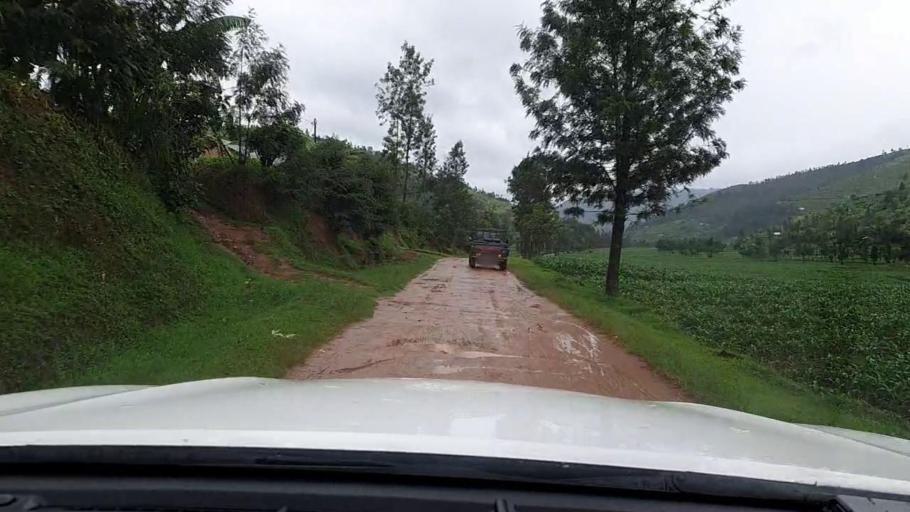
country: RW
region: Northern Province
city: Byumba
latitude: -1.7418
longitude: 29.9444
